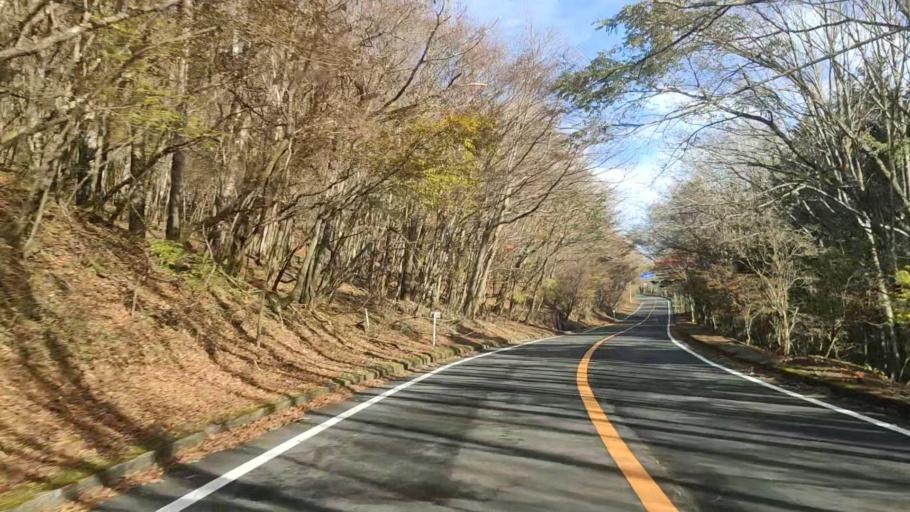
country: JP
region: Shizuoka
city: Fuji
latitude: 35.3026
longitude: 138.7445
